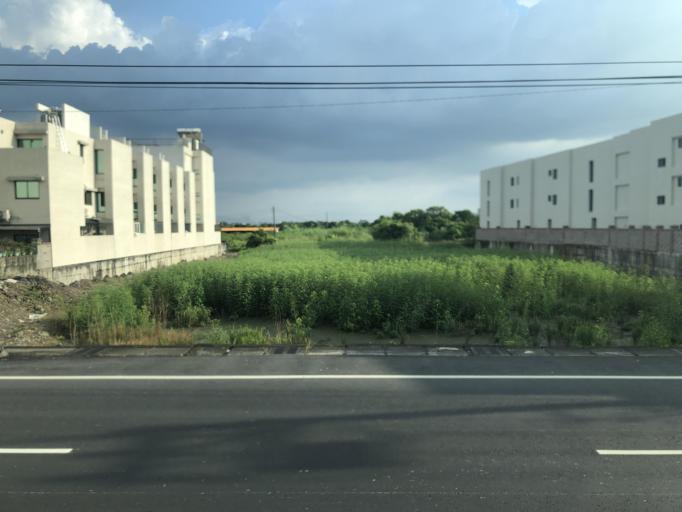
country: TW
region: Taiwan
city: Yujing
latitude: 22.9023
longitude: 120.5333
